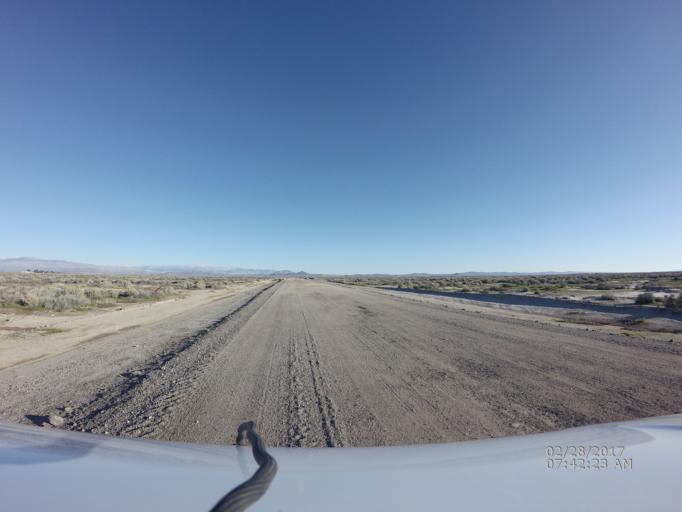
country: US
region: California
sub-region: Kern County
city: Rosamond
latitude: 34.7837
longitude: -118.1847
